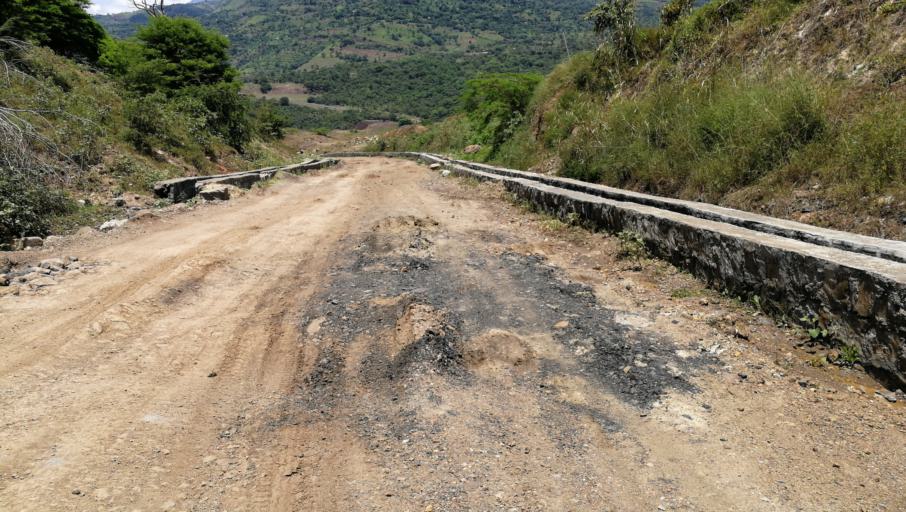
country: ET
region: Southern Nations, Nationalities, and People's Region
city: Areka
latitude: 6.9272
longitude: 37.3067
